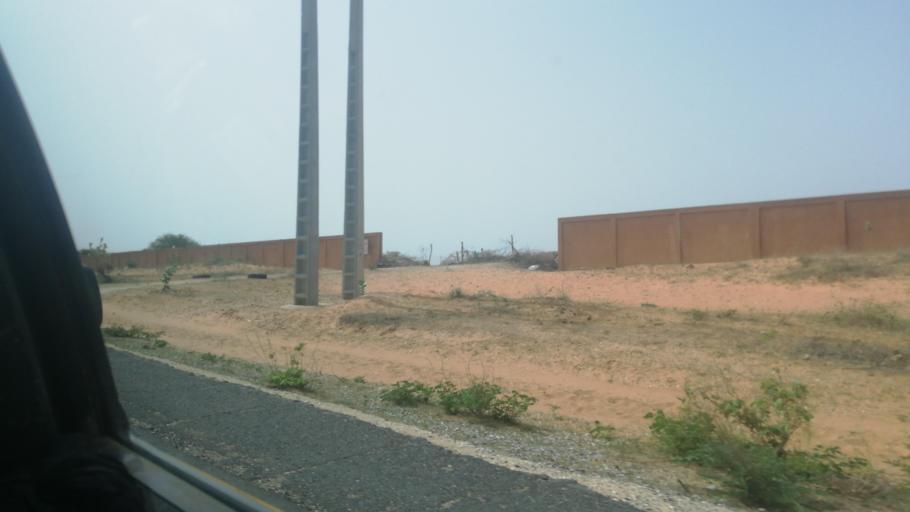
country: SN
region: Saint-Louis
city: Saint-Louis
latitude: 16.0764
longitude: -16.3799
